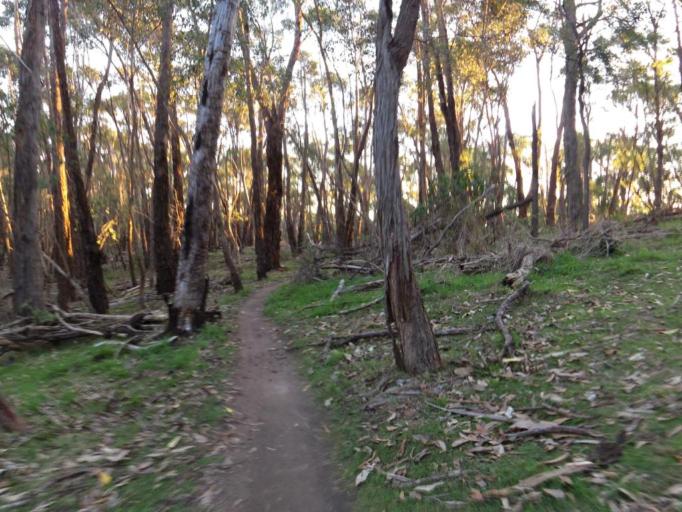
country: AU
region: Victoria
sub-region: Yarra Ranges
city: Lysterfield
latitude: -37.9425
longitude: 145.3052
